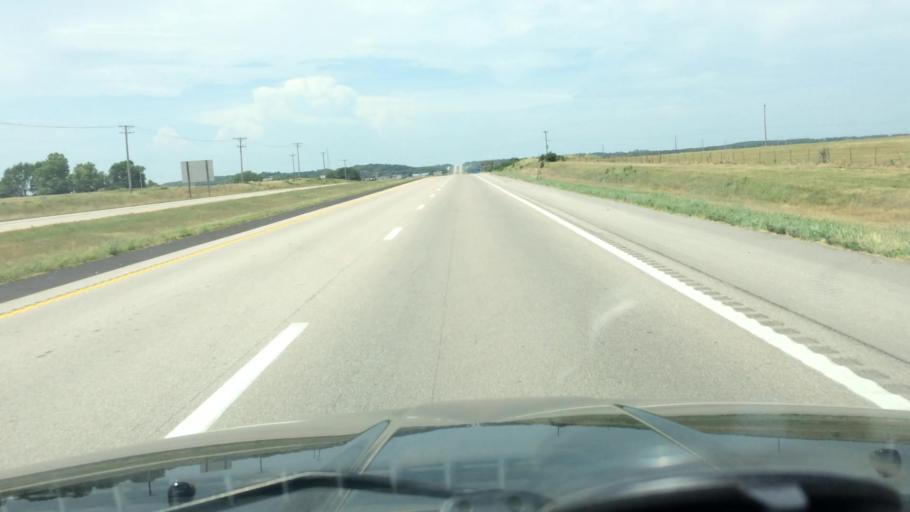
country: US
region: Missouri
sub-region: Polk County
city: Bolivar
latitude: 37.6034
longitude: -93.4402
